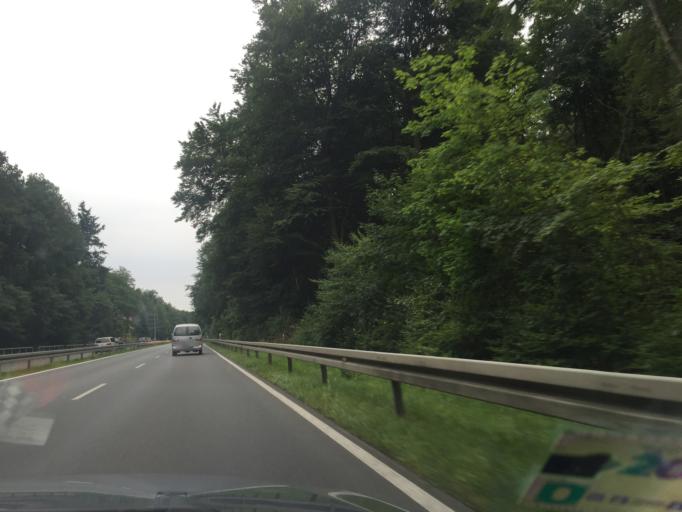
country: DE
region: Brandenburg
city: Wandlitz
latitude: 52.7385
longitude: 13.4873
